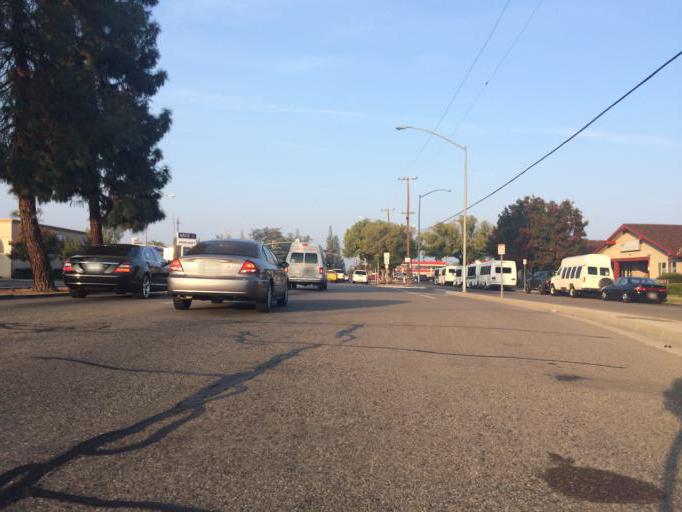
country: US
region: California
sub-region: Fresno County
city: Fresno
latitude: 36.7942
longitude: -119.7528
